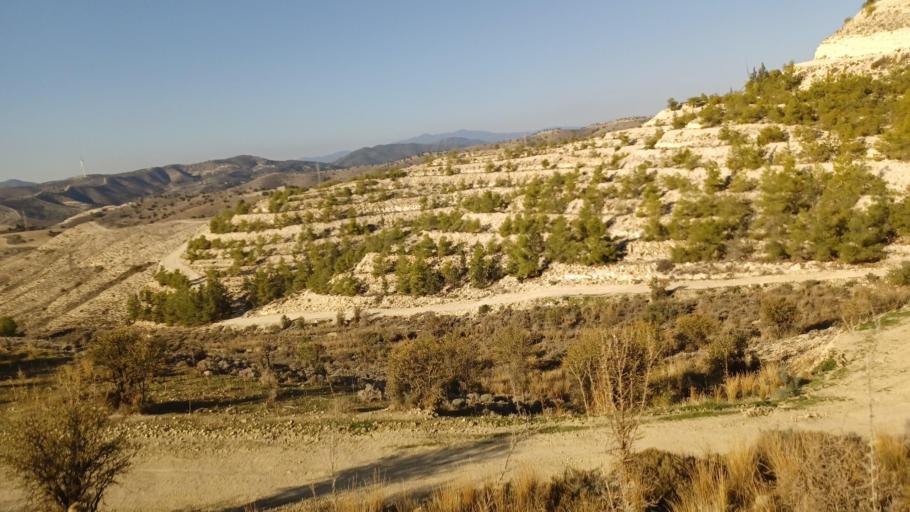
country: CY
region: Larnaka
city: Psevdas
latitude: 34.9512
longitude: 33.5083
